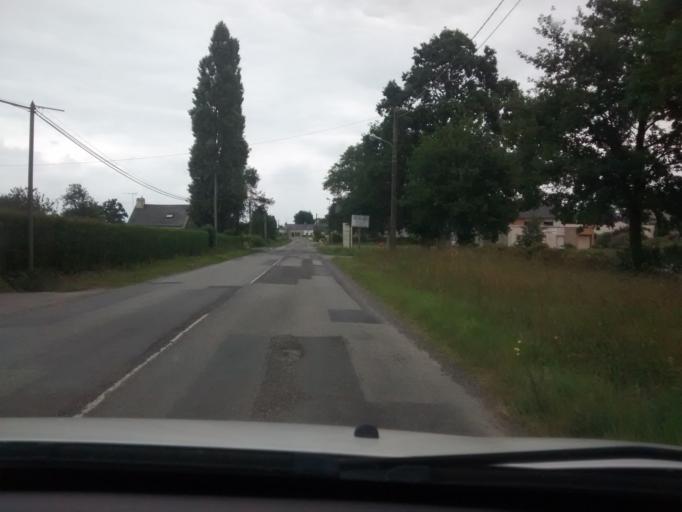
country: FR
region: Brittany
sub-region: Departement d'Ille-et-Vilaine
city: La Bouexiere
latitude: 48.1728
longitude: -1.4362
